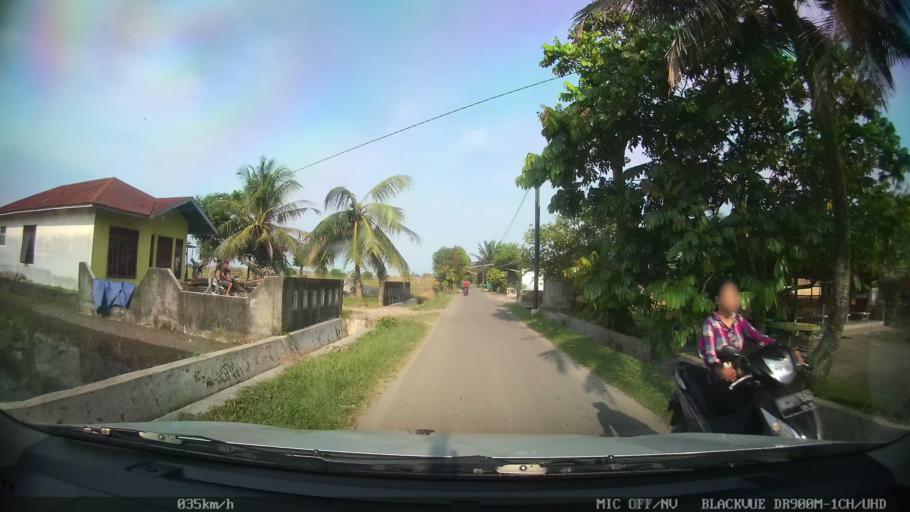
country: ID
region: North Sumatra
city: Binjai
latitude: 3.6210
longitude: 98.5256
